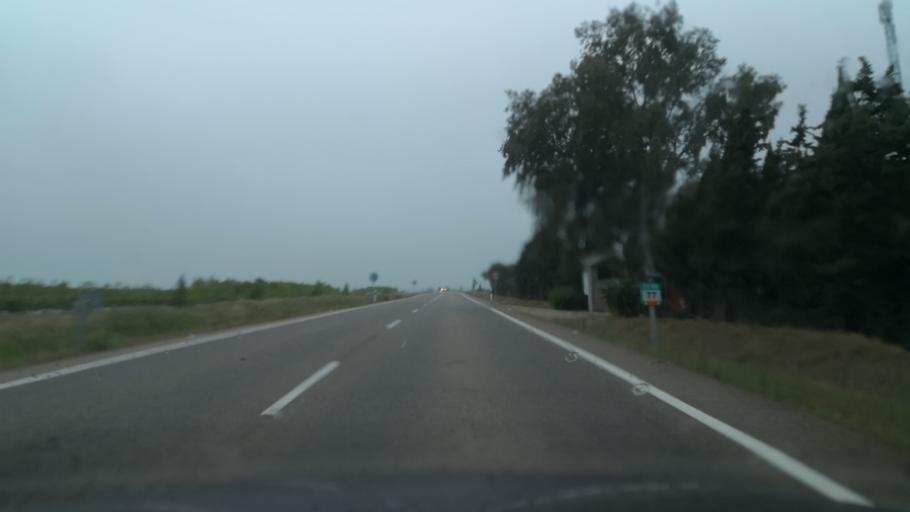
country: ES
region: Extremadura
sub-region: Provincia de Badajoz
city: Badajoz
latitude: 38.9476
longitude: -6.9148
